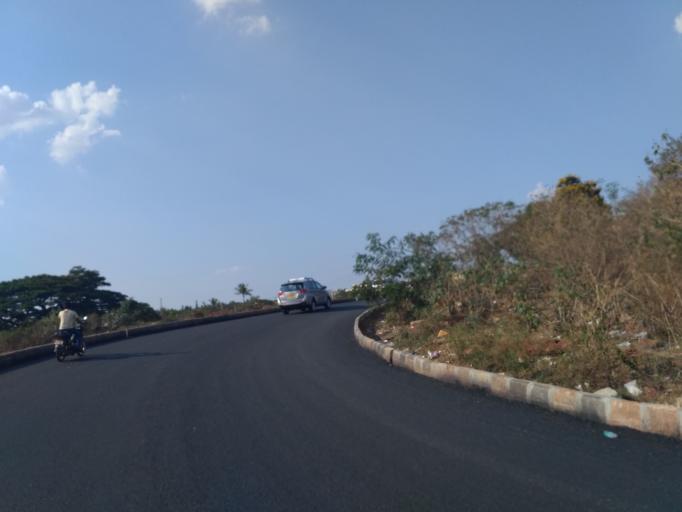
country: IN
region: Karnataka
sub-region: Bangalore Urban
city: Yelahanka
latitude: 13.0432
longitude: 77.5392
